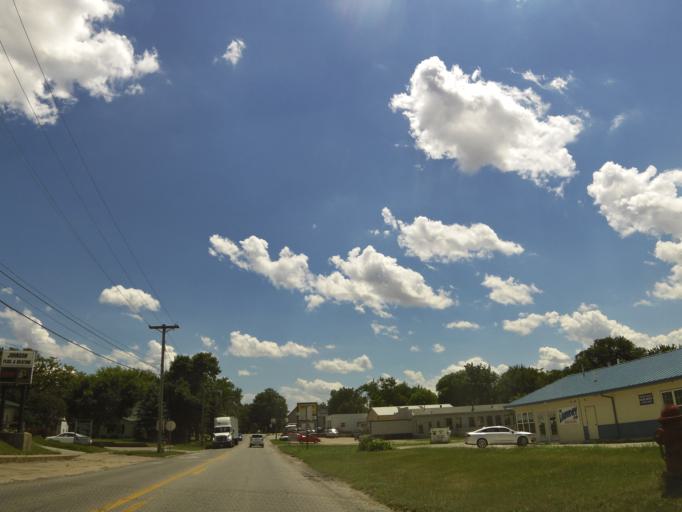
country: US
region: Iowa
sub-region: Buchanan County
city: Independence
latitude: 42.4774
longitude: -91.8894
